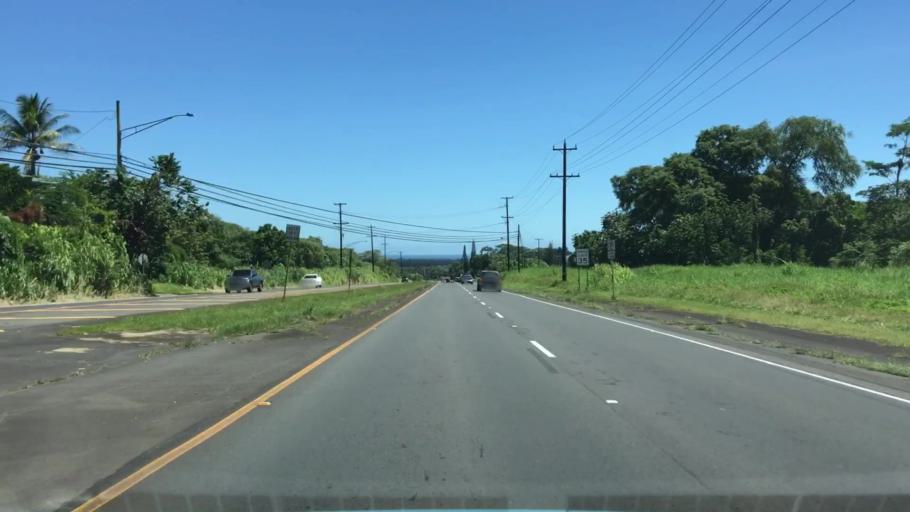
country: US
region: Hawaii
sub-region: Hawaii County
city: Kea'au
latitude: 19.6145
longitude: -155.0467
